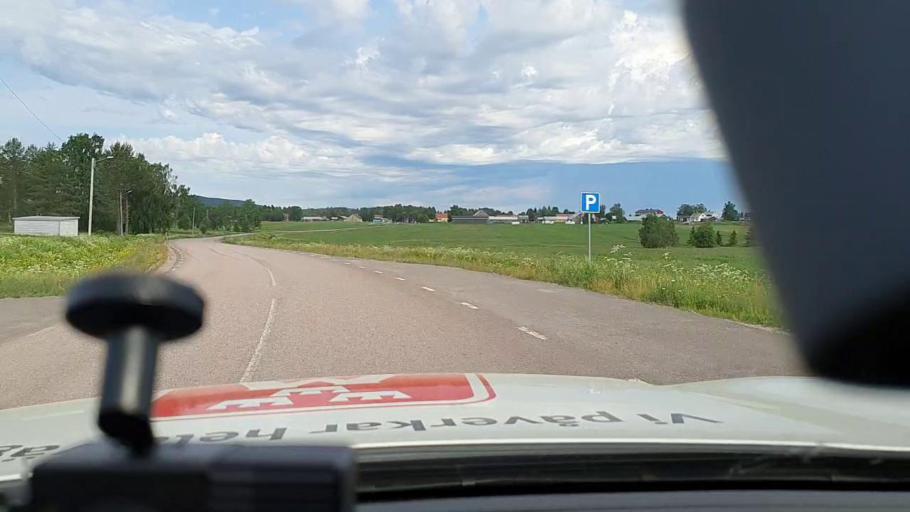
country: SE
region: Norrbotten
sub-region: Bodens Kommun
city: Saevast
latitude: 65.7046
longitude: 21.7676
